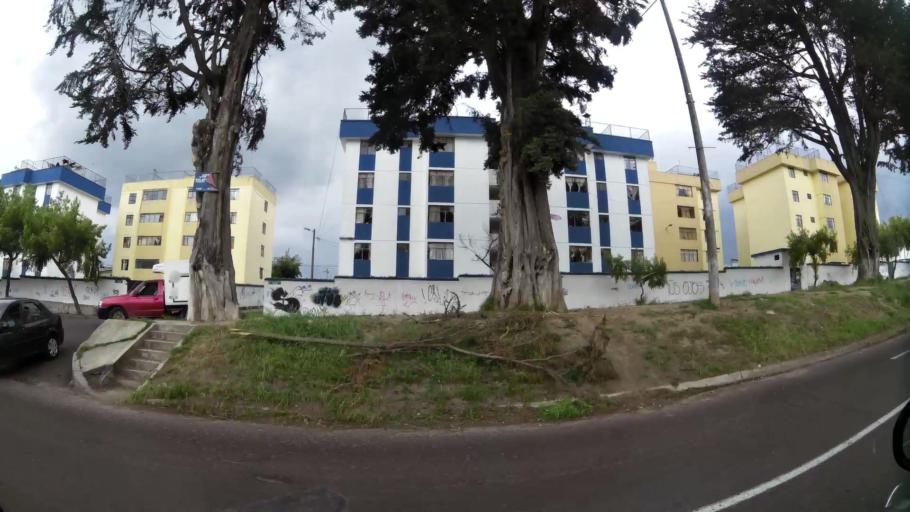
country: EC
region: Pichincha
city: Quito
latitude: -0.0864
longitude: -78.4744
